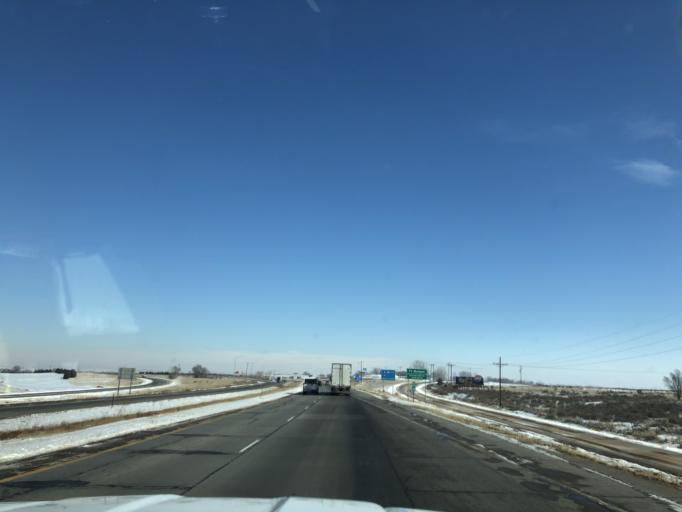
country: US
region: Colorado
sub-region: Morgan County
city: Fort Morgan
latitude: 40.2475
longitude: -103.8894
